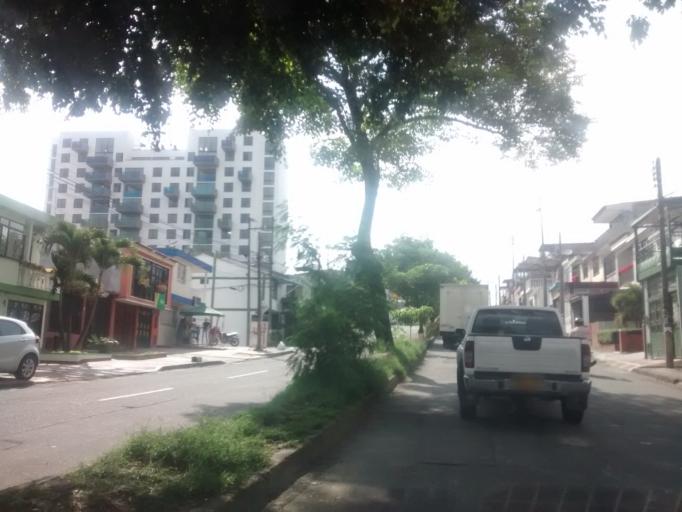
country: CO
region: Tolima
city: Ibague
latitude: 4.4419
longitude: -75.2006
